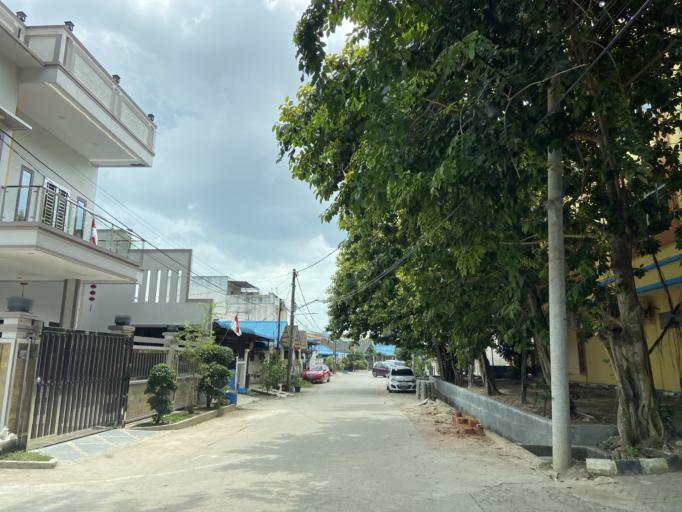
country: SG
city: Singapore
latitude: 1.1246
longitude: 104.0117
